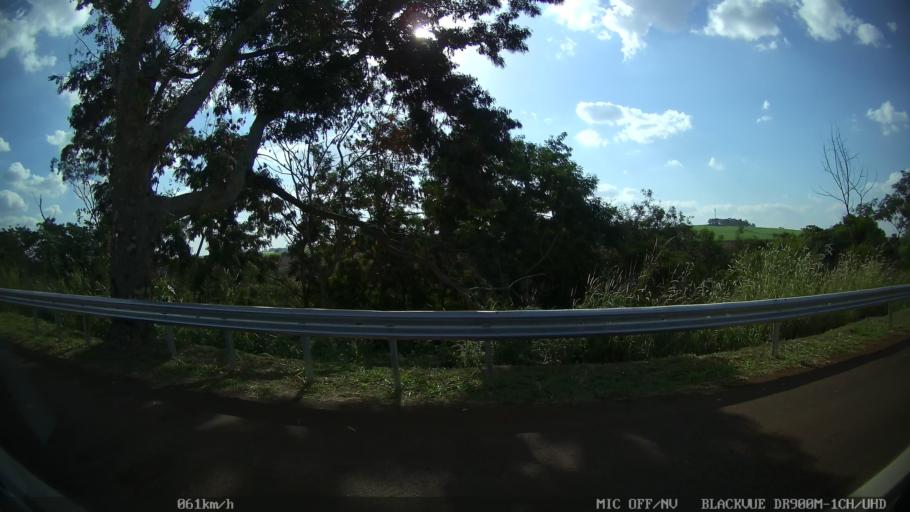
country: BR
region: Sao Paulo
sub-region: Ribeirao Preto
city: Ribeirao Preto
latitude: -21.1967
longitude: -47.8755
